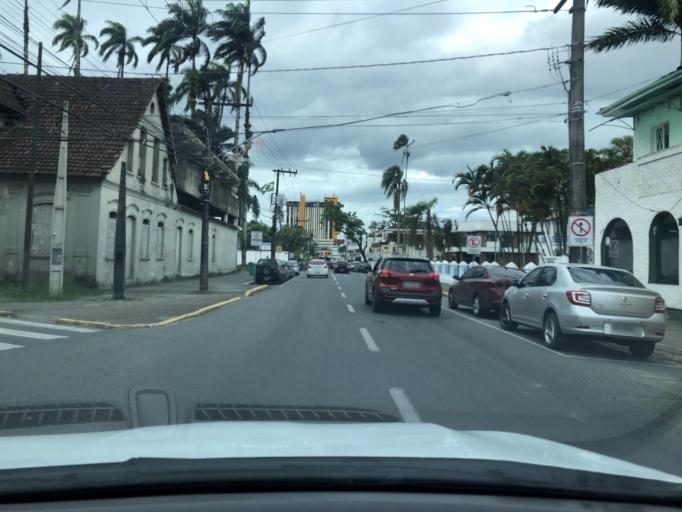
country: BR
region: Santa Catarina
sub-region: Joinville
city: Joinville
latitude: -26.3042
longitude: -48.8438
